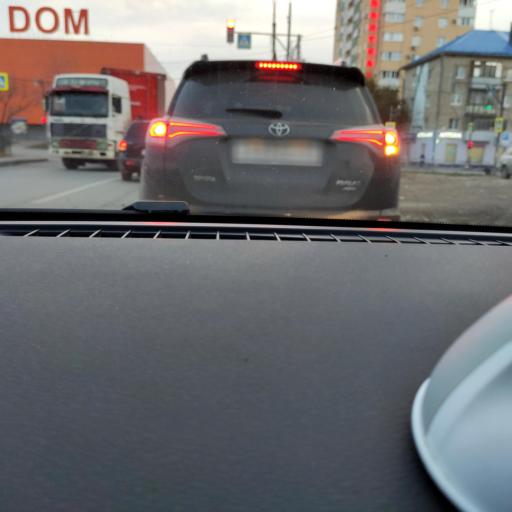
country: RU
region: Samara
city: Samara
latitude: 53.2079
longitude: 50.2003
